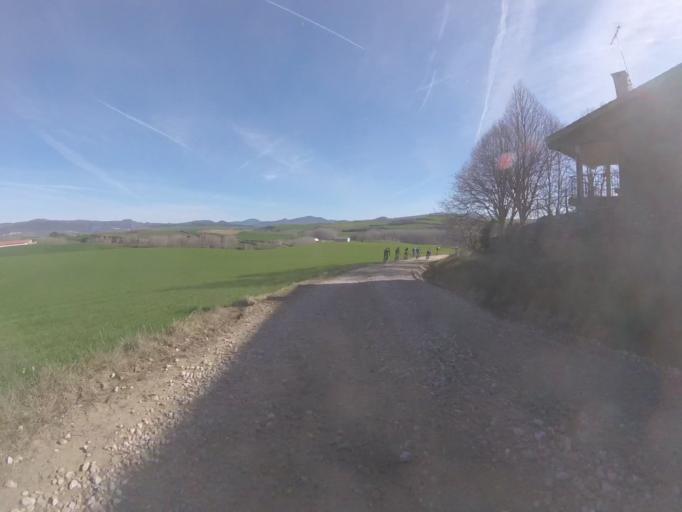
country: ES
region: Navarre
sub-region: Provincia de Navarra
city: Villatuerta
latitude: 42.6925
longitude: -1.9988
